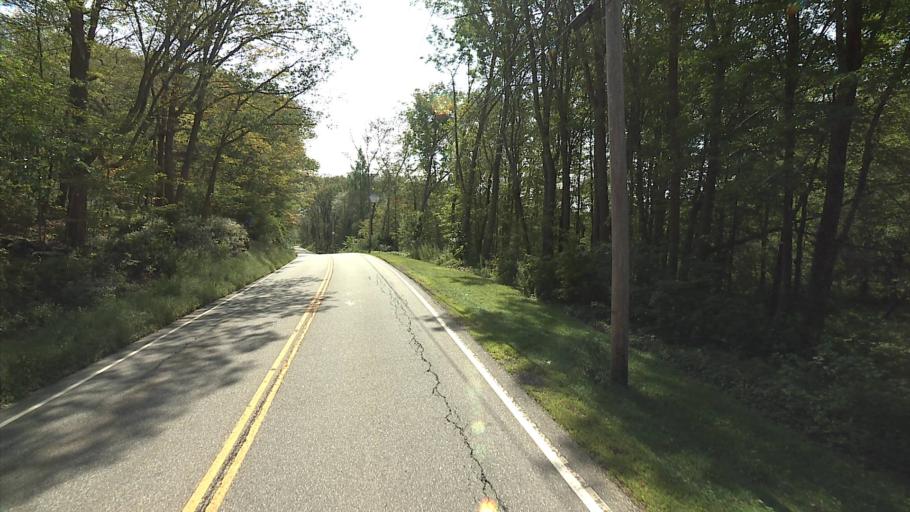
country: US
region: Connecticut
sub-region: Windham County
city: East Brooklyn
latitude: 41.8094
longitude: -71.9545
